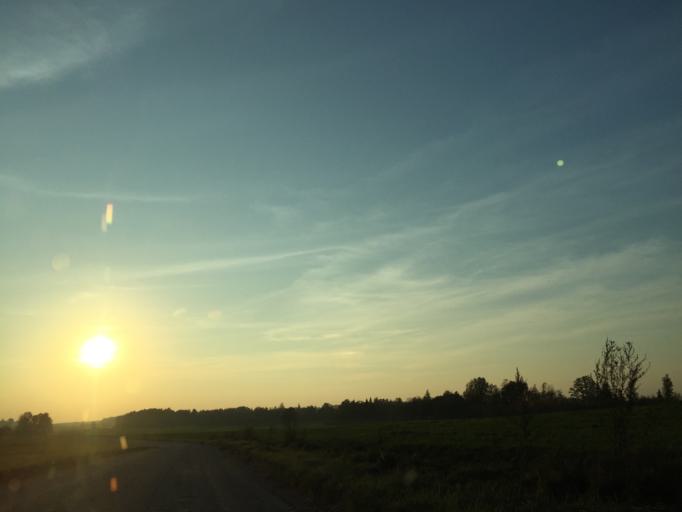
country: LV
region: Vainode
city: Vainode
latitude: 56.4858
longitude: 21.7615
